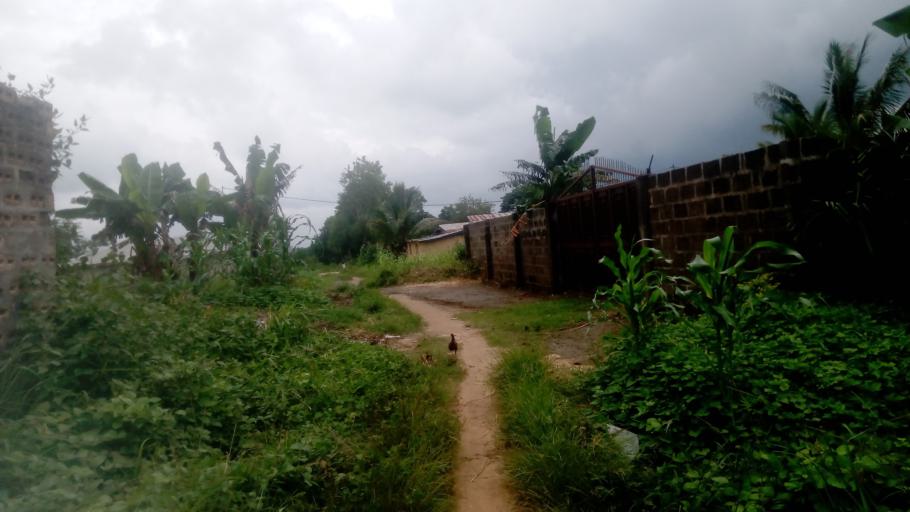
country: SL
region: Northern Province
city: Lunsar
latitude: 8.6771
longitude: -12.5401
